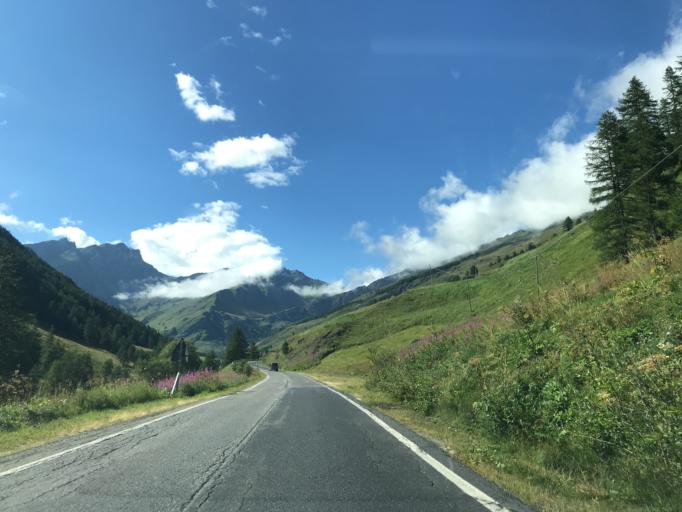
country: IT
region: Piedmont
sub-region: Provincia di Cuneo
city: Pontechianale
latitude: 44.6301
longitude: 7.0193
